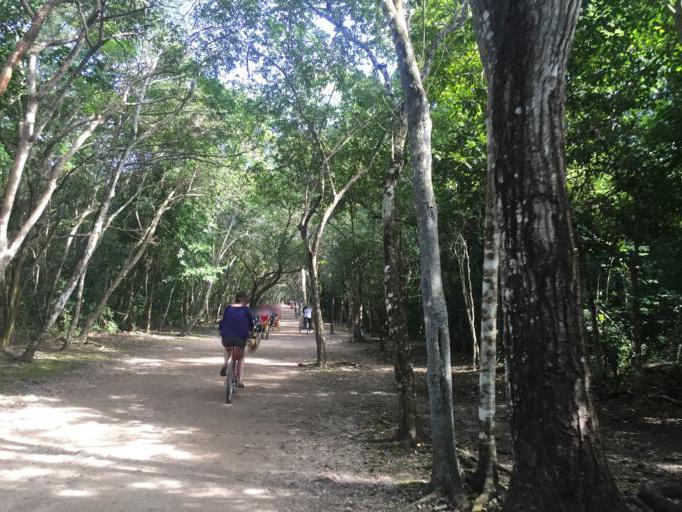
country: MX
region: Quintana Roo
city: Coba
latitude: 20.4903
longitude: -87.7288
